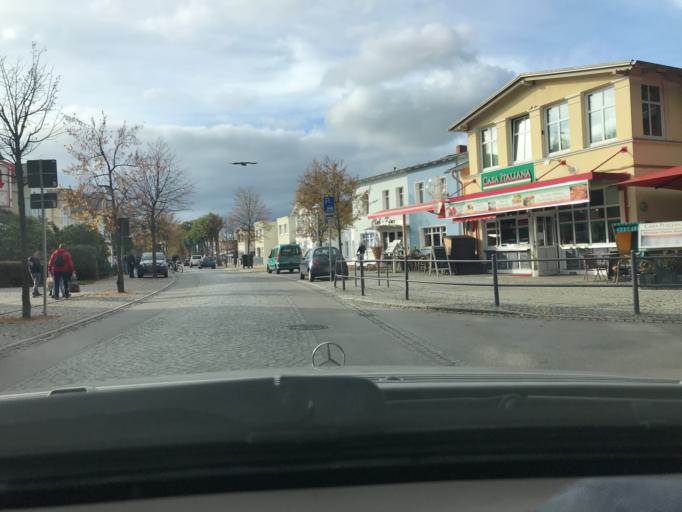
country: DE
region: Mecklenburg-Vorpommern
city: Ostseebad Zinnowitz
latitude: 54.0783
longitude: 13.9117
